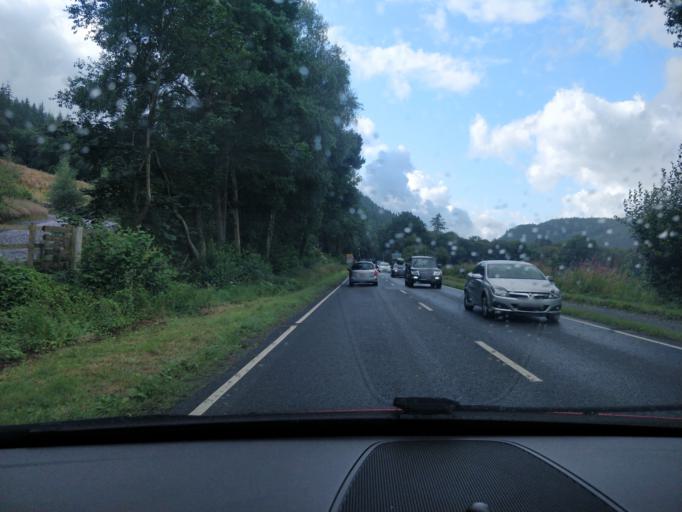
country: GB
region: Wales
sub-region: Conwy
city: Betws-y-Coed
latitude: 53.1006
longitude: -3.7876
